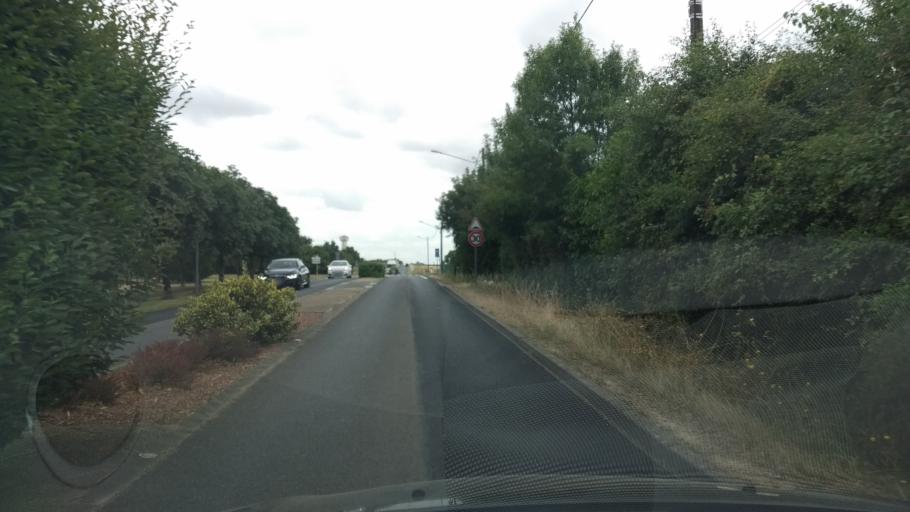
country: FR
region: Poitou-Charentes
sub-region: Departement de la Vienne
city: Roches-Premarie-Andille
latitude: 46.4778
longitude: 0.3692
